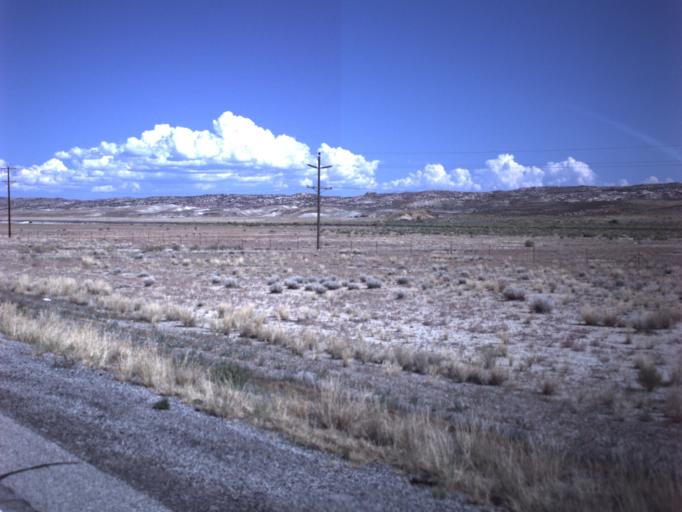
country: US
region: Utah
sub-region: Grand County
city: Moab
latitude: 38.7655
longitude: -109.7444
